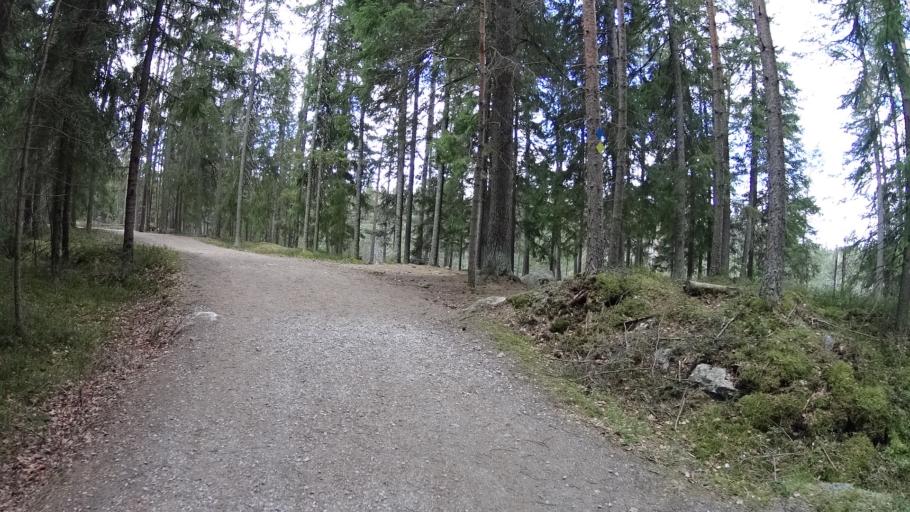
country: FI
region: Uusimaa
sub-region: Helsinki
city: Espoo
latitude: 60.2694
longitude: 24.6160
